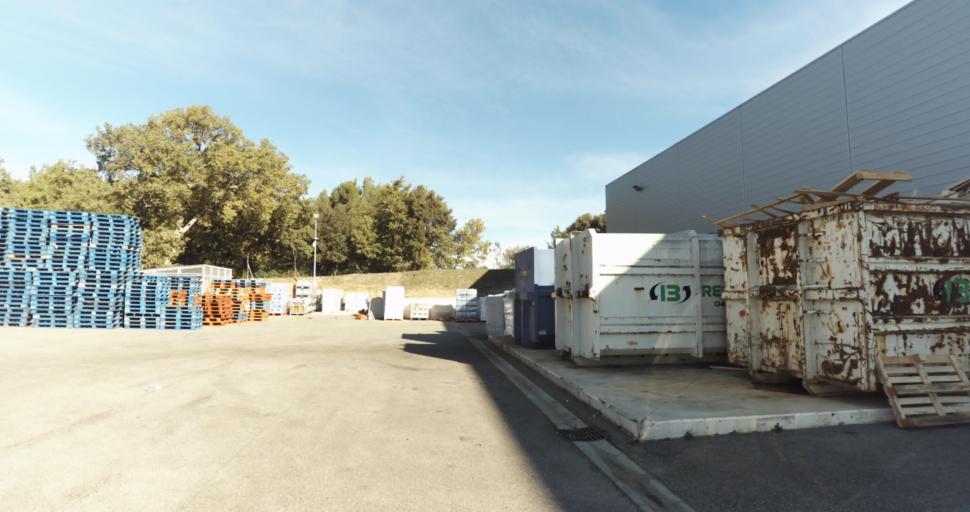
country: FR
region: Provence-Alpes-Cote d'Azur
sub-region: Departement des Bouches-du-Rhone
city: Venelles
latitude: 43.5833
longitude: 5.4656
